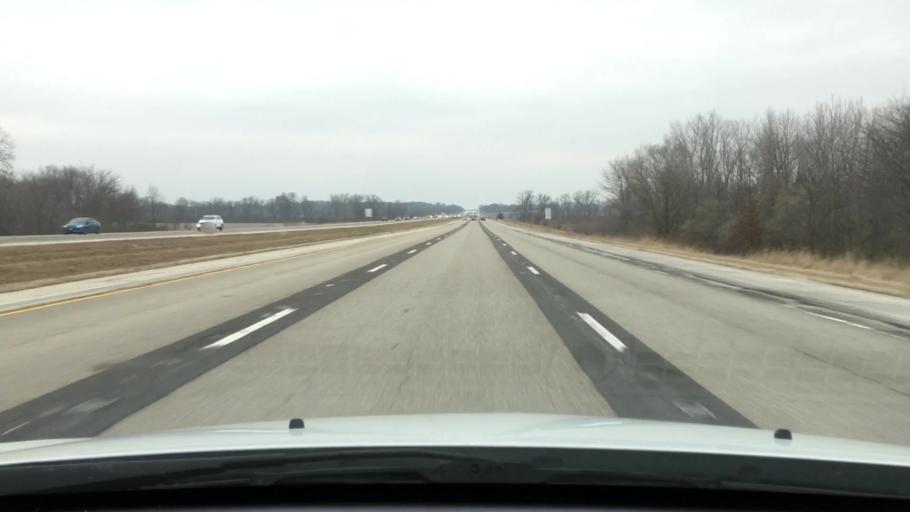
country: US
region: Illinois
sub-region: Logan County
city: Lincoln
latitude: 40.1208
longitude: -89.4165
